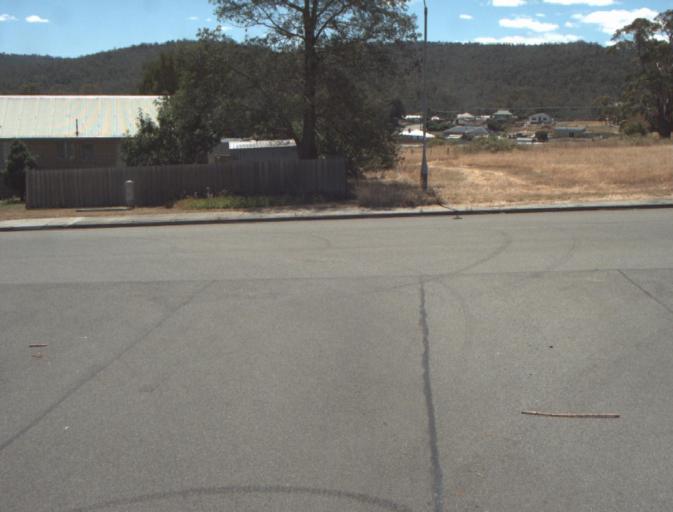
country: AU
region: Tasmania
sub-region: Launceston
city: Mayfield
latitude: -41.3743
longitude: 147.1384
